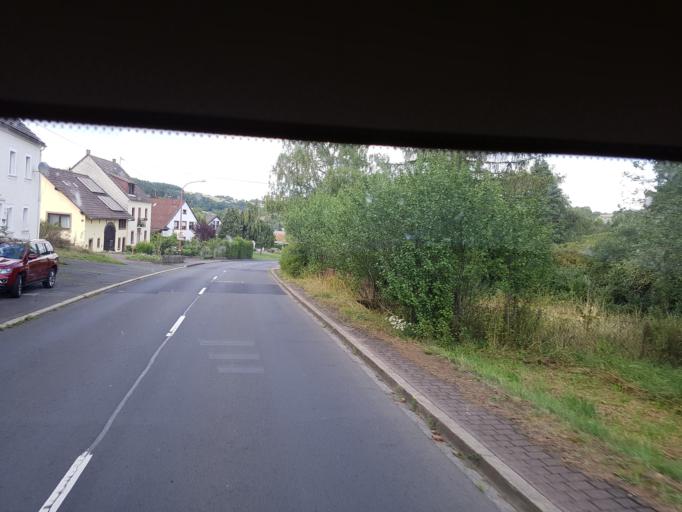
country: DE
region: Rheinland-Pfalz
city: Dreis-Bruck
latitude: 50.2615
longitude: 6.7891
